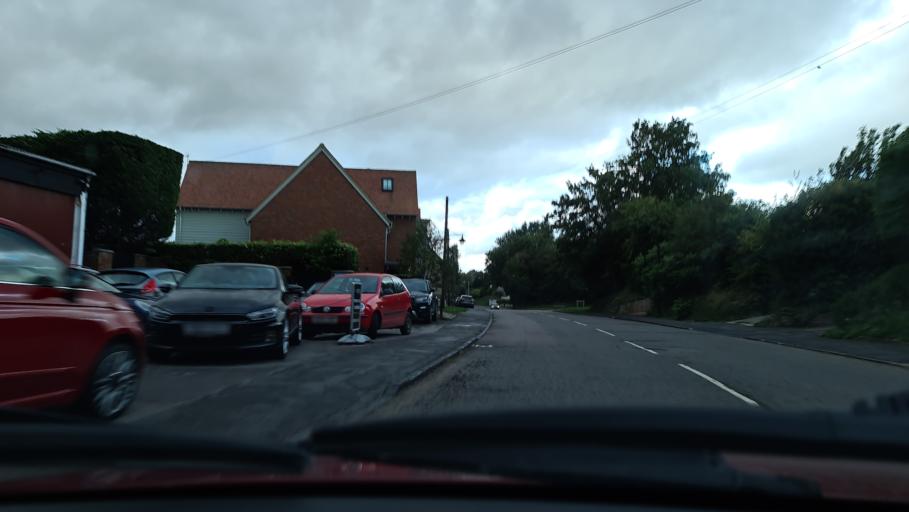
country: GB
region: England
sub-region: Buckinghamshire
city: Long Crendon
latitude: 51.7731
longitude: -0.9970
